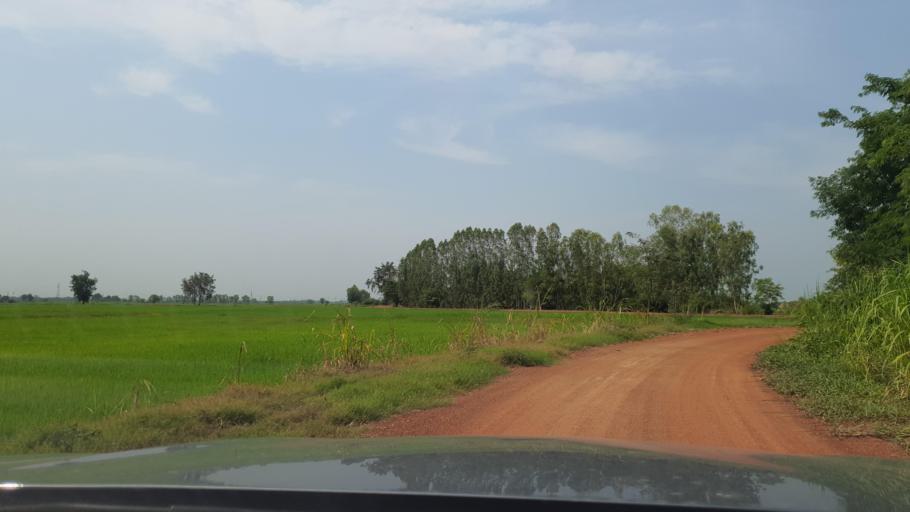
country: TH
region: Phitsanulok
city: Bang Rakam
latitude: 16.7973
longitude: 100.1076
